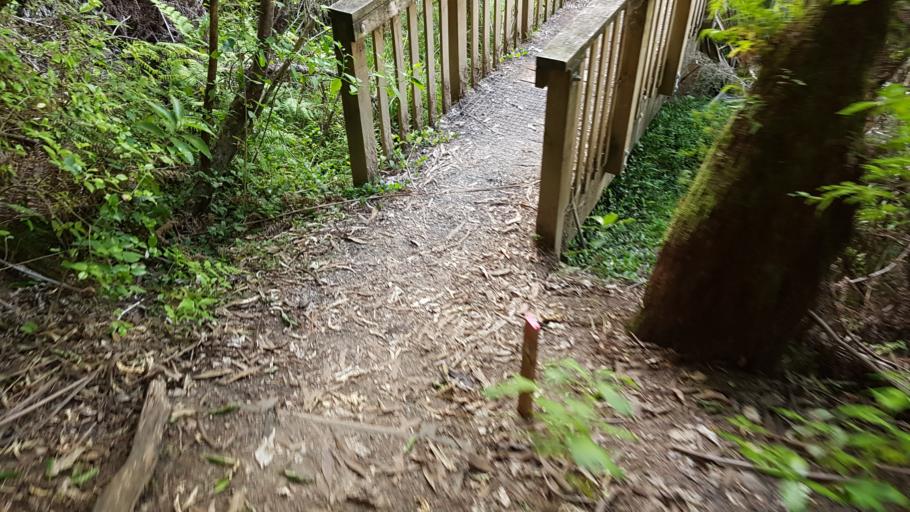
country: NZ
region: Auckland
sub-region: Auckland
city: North Shore
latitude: -36.8189
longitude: 174.7200
